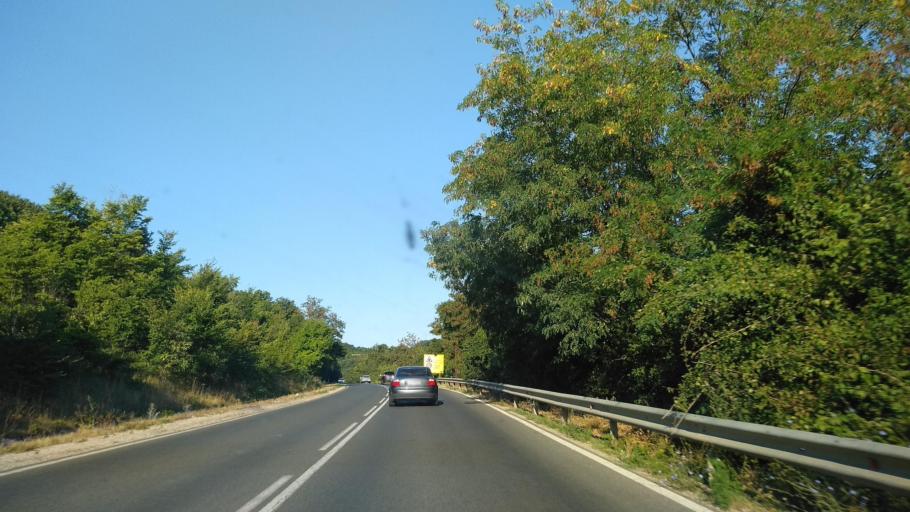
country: BG
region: Veliko Turnovo
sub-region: Obshtina Pavlikeni
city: Byala Cherkva
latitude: 43.0656
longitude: 25.2940
